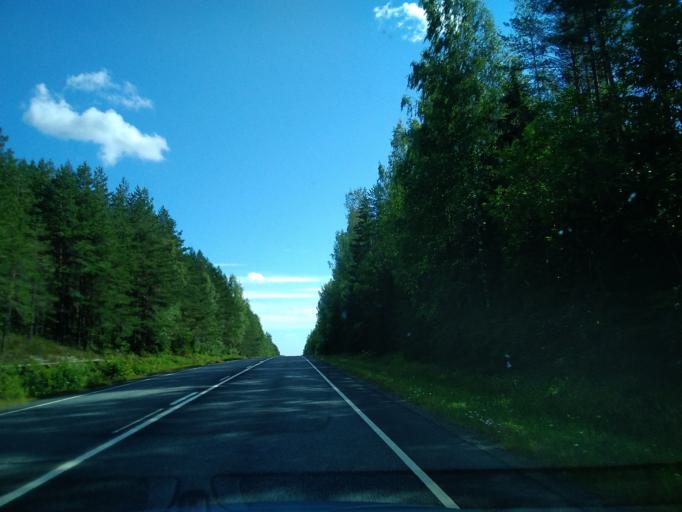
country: FI
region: Haeme
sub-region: Haemeenlinna
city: Renko
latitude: 60.8412
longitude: 24.1043
